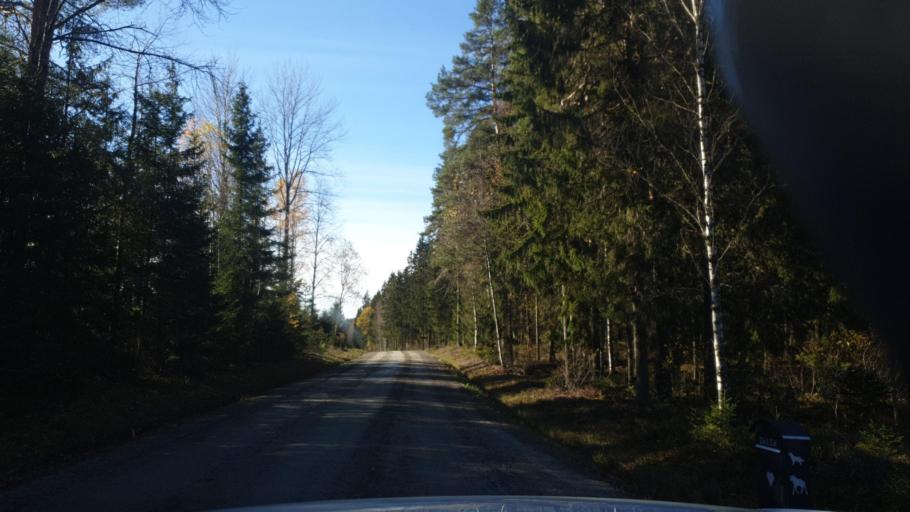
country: SE
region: Vaermland
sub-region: Karlstads Kommun
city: Edsvalla
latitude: 59.4891
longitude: 13.0600
